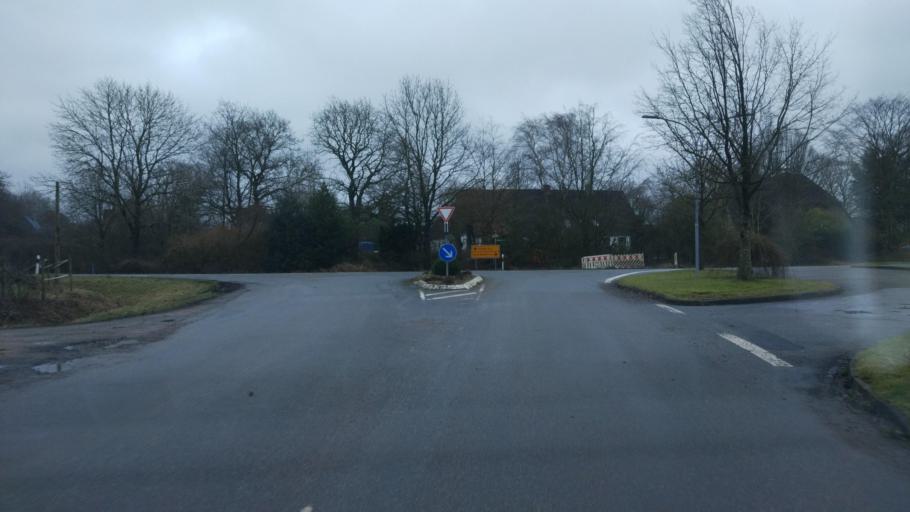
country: DE
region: Schleswig-Holstein
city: Ellingstedt
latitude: 54.4832
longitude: 9.4091
